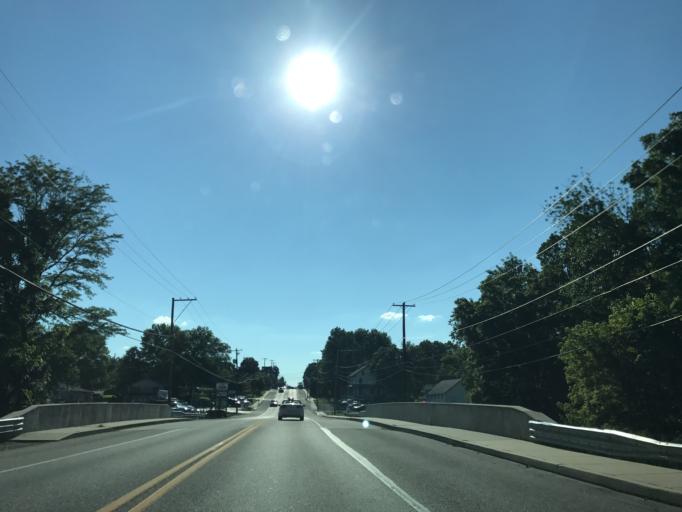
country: US
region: Pennsylvania
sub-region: Lancaster County
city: Mount Joy
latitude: 40.1090
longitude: -76.4896
